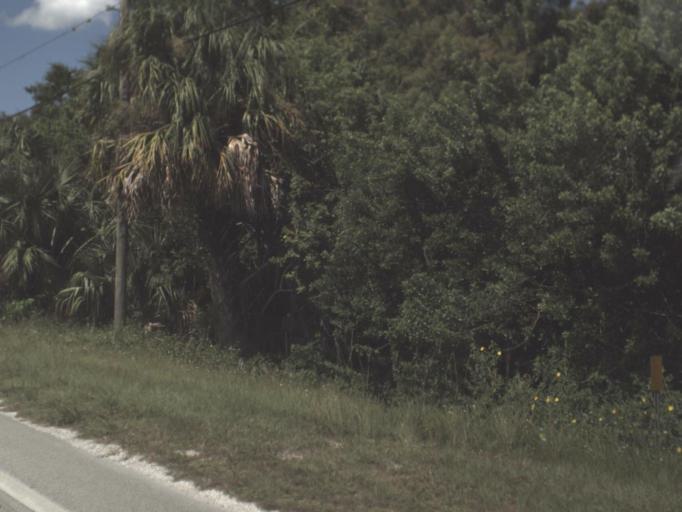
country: US
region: Florida
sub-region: Okeechobee County
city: Taylor Creek
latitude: 27.1889
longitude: -80.7488
